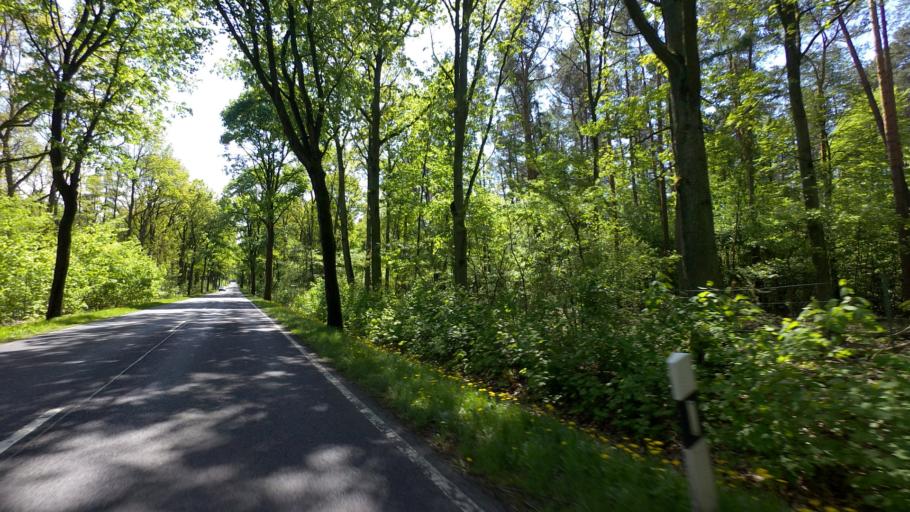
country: DE
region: Brandenburg
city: Schulzendorf
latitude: 52.3261
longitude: 13.5830
